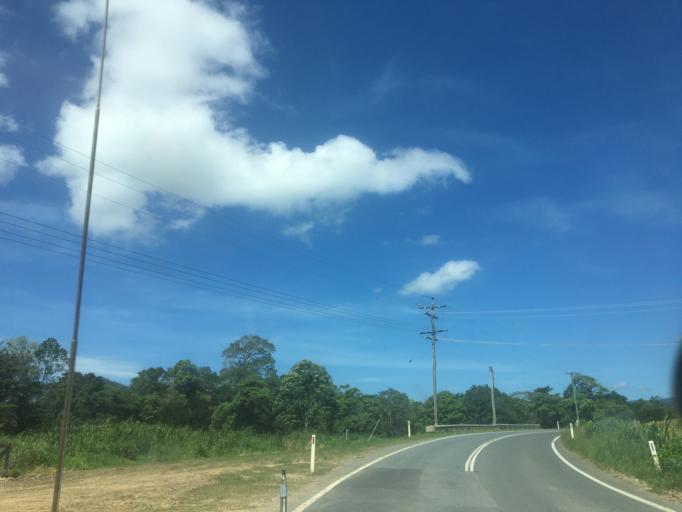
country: AU
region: Queensland
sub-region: Cairns
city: Woree
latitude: -17.0672
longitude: 145.7414
